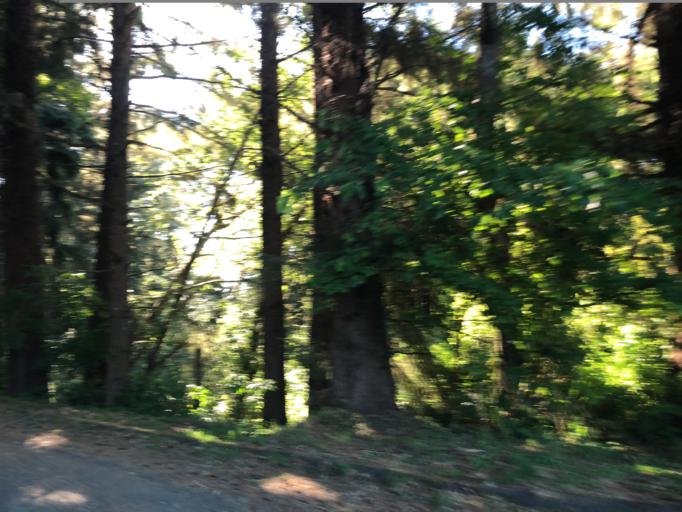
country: US
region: California
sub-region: Humboldt County
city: Westhaven-Moonstone
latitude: 41.0614
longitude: -124.1432
